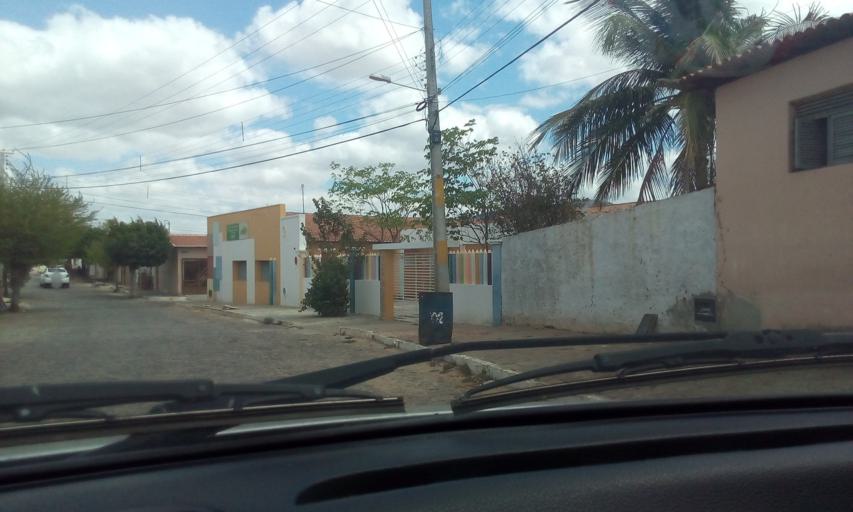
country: BR
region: Rio Grande do Norte
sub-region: Currais Novos
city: Currais Novos
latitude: -6.2155
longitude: -36.6808
